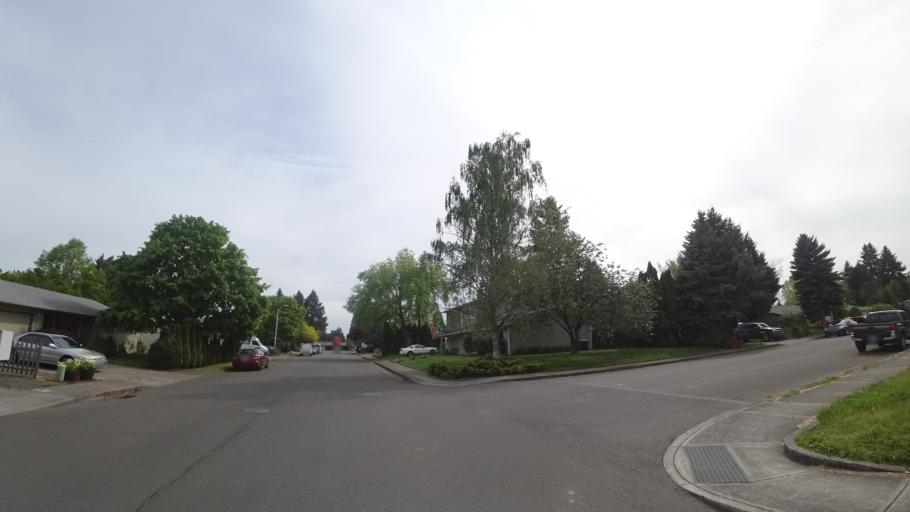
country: US
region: Oregon
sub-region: Washington County
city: Hillsboro
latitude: 45.5185
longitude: -122.9443
